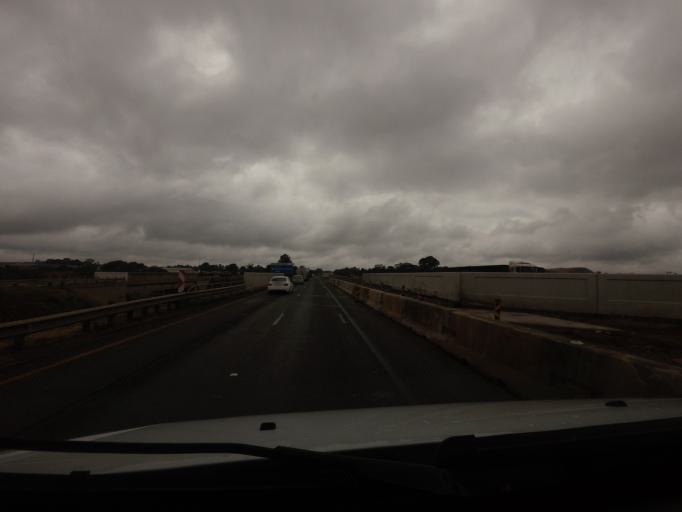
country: ZA
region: Mpumalanga
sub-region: Nkangala District Municipality
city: Witbank
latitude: -25.8847
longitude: 29.2018
